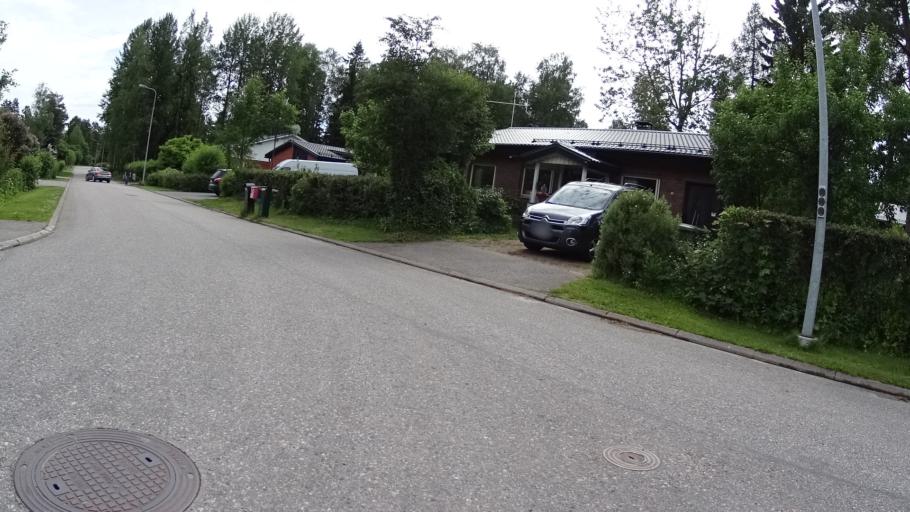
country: FI
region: Uusimaa
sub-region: Helsinki
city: Kilo
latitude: 60.2522
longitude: 24.8066
